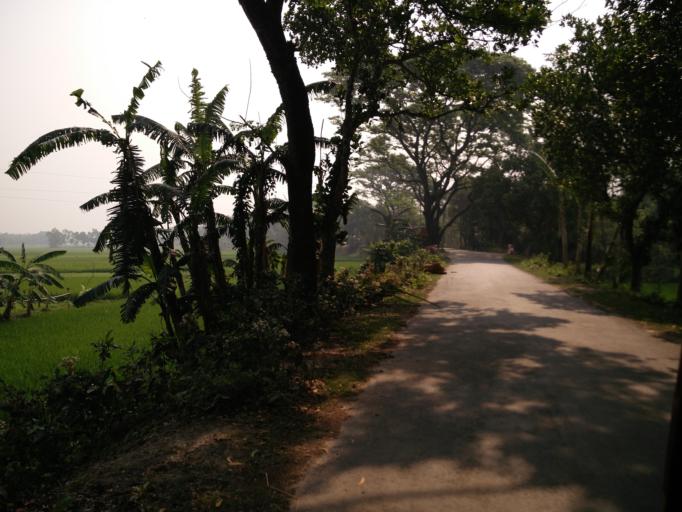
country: BD
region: Dhaka
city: Muktagacha
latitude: 24.9091
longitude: 90.1630
